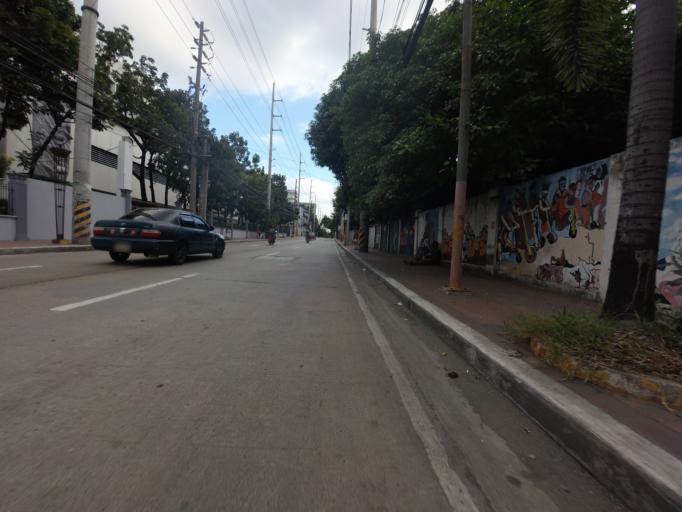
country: PH
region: Metro Manila
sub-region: City of Manila
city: Quiapo
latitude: 14.5872
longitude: 120.9853
